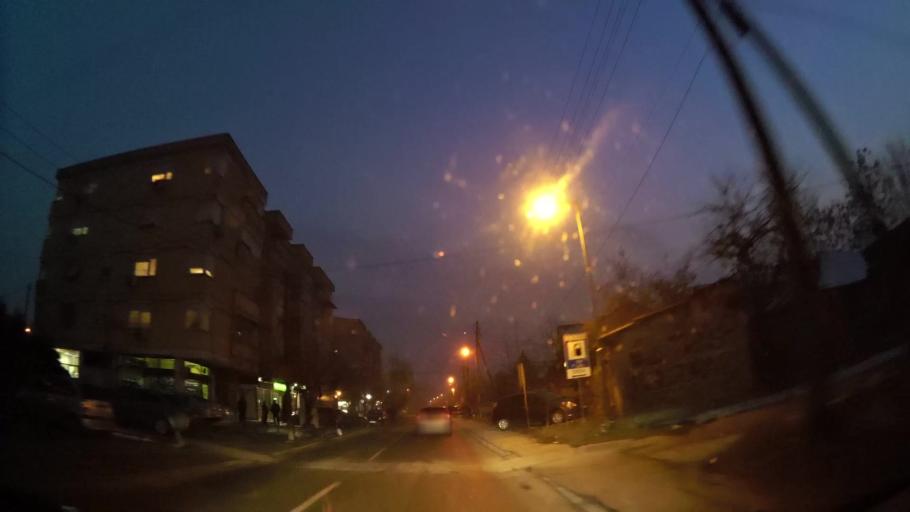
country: MK
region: Kisela Voda
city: Kisela Voda
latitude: 41.9970
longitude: 21.4998
